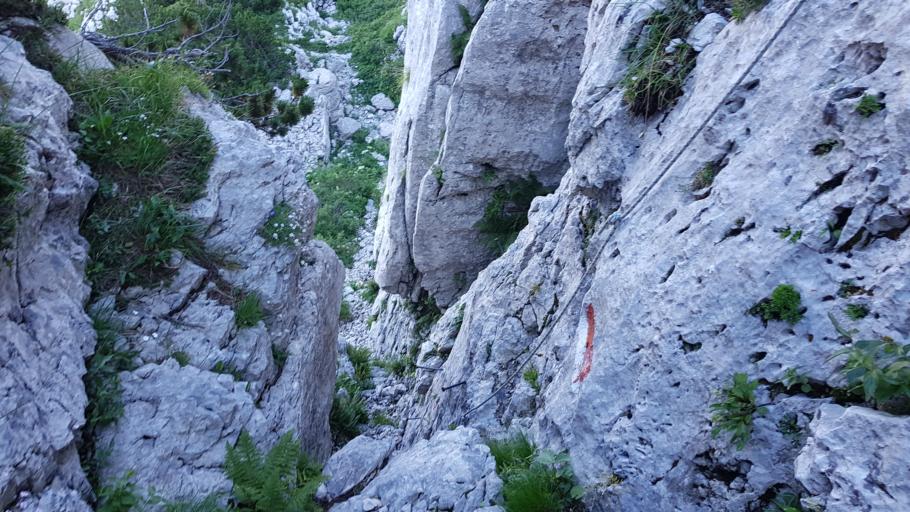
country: SI
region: Bovec
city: Bovec
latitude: 46.3874
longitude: 13.5283
